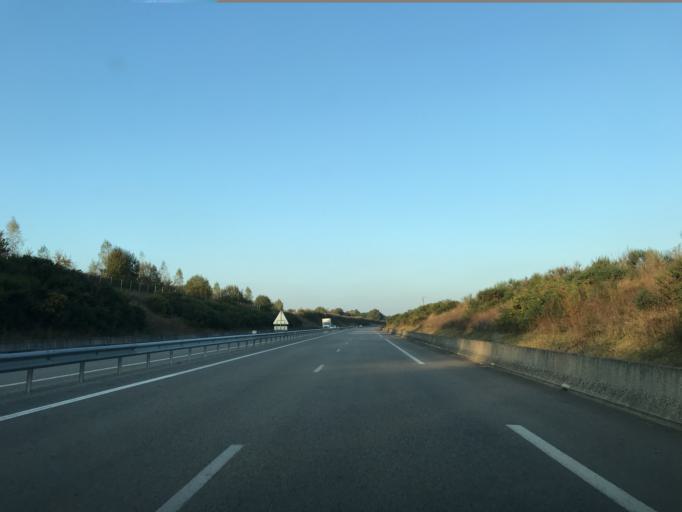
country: FR
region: Lower Normandy
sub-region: Departement de l'Orne
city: Sees
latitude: 48.4933
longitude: 0.2964
